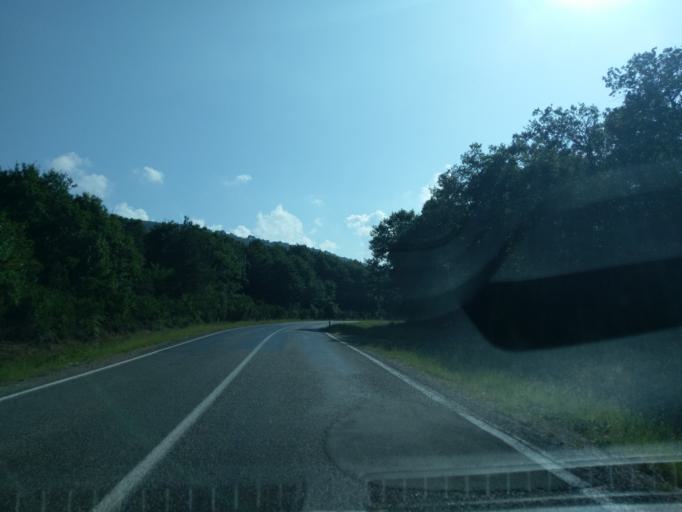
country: TR
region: Sinop
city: Yenikonak
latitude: 41.9453
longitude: 34.7420
